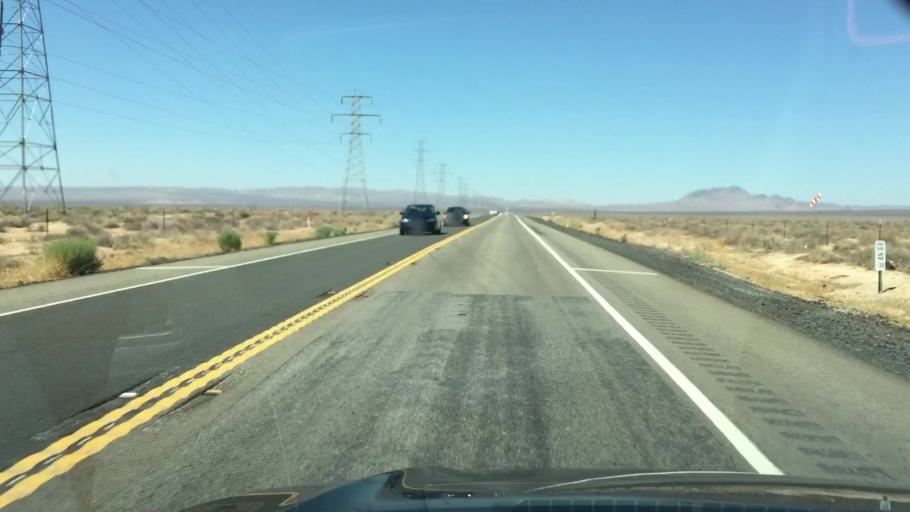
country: US
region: California
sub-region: Kern County
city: Boron
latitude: 35.1463
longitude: -117.5843
